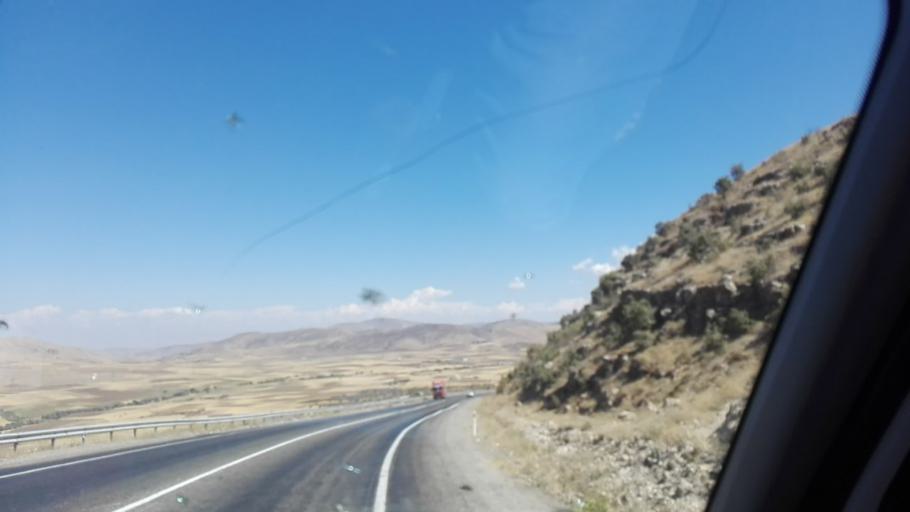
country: TR
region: Batman
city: Gerdzhyush
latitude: 37.5620
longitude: 41.3615
